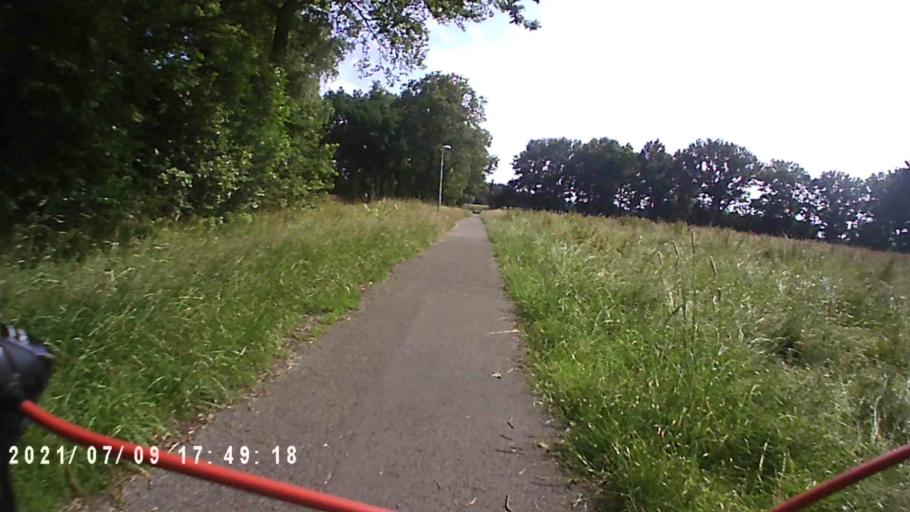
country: NL
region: Groningen
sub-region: Gemeente Vlagtwedde
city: Vlagtwedde
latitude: 53.0752
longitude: 7.0772
